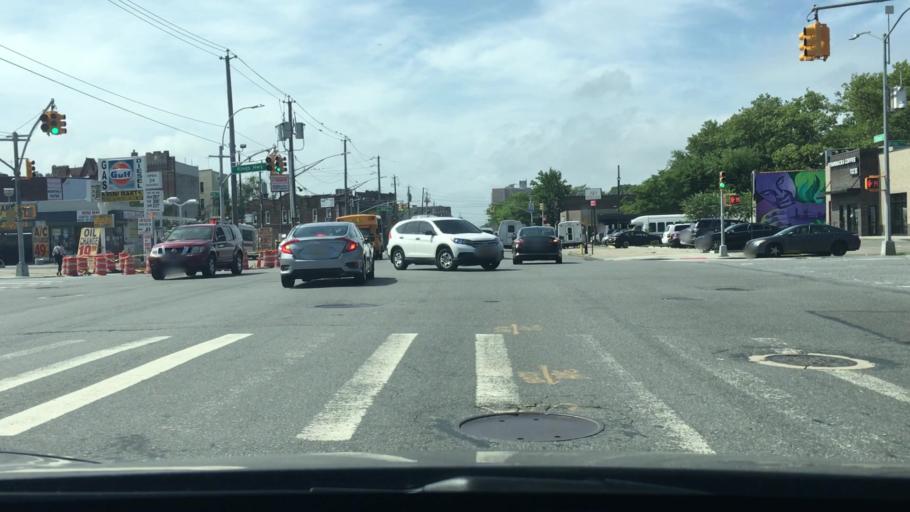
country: US
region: New York
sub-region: Kings County
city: Brooklyn
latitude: 40.6223
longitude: -73.9364
